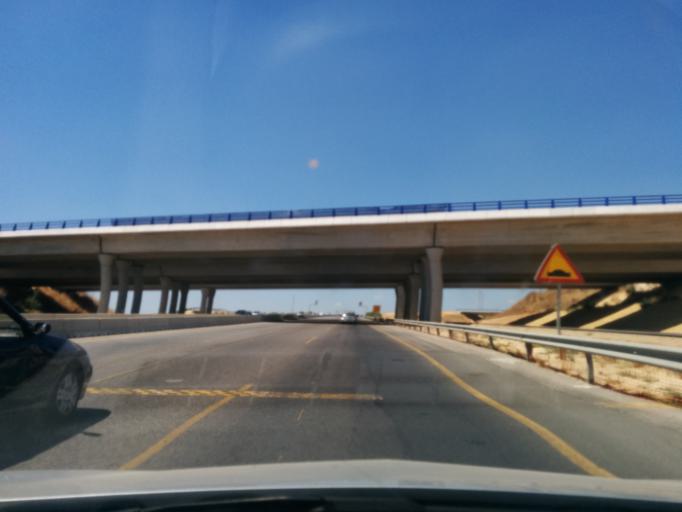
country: ES
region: Andalusia
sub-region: Provincia de Sevilla
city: Espartinas
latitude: 37.3693
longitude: -6.1035
